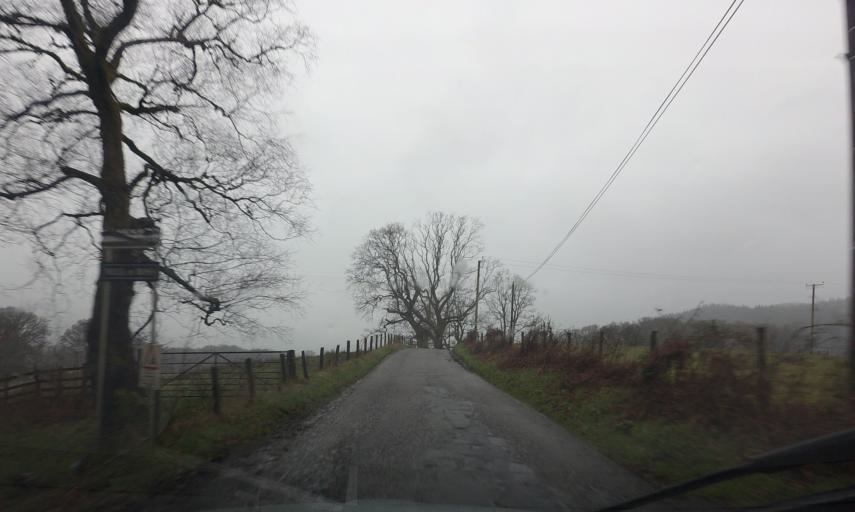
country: GB
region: Scotland
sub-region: West Dunbartonshire
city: Balloch
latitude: 56.1379
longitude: -4.6165
